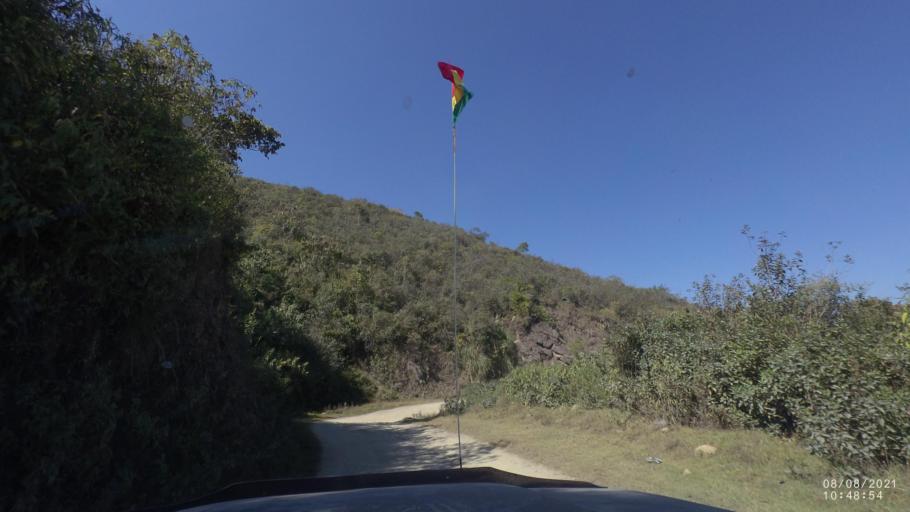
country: BO
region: La Paz
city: Quime
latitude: -16.7175
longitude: -66.7057
